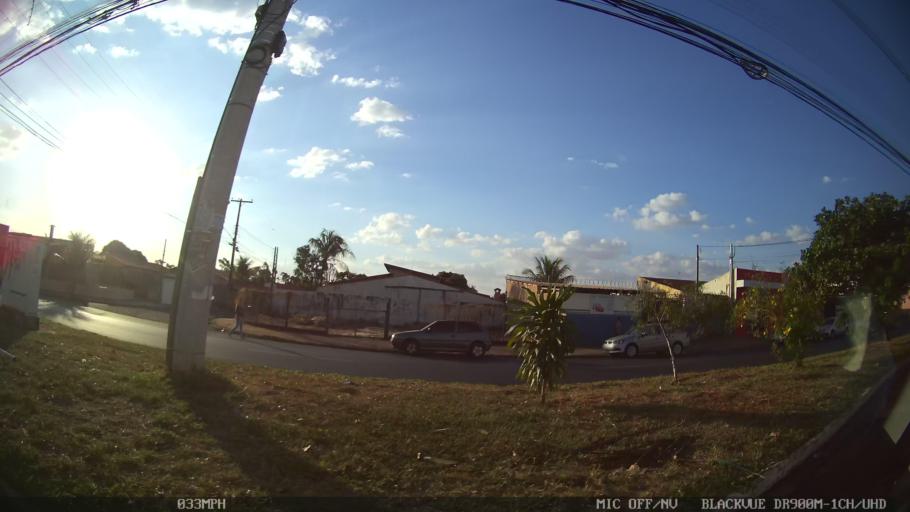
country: BR
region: Sao Paulo
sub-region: Ribeirao Preto
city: Ribeirao Preto
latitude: -21.1618
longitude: -47.7377
